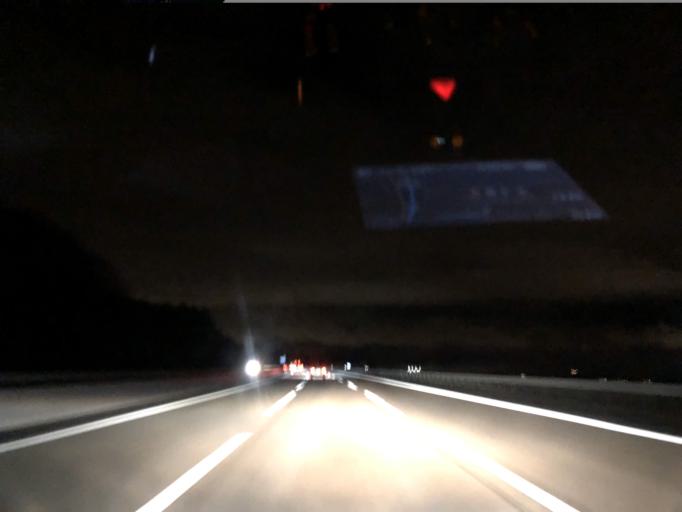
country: DE
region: Hesse
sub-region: Regierungsbezirk Darmstadt
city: Seligenstadt
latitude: 50.0453
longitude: 8.9298
